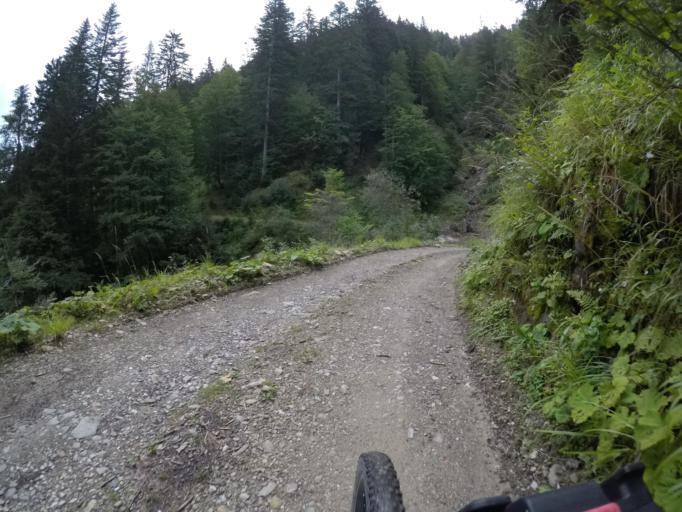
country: IT
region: Friuli Venezia Giulia
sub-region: Provincia di Udine
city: Pontebba
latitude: 46.5166
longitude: 13.2297
